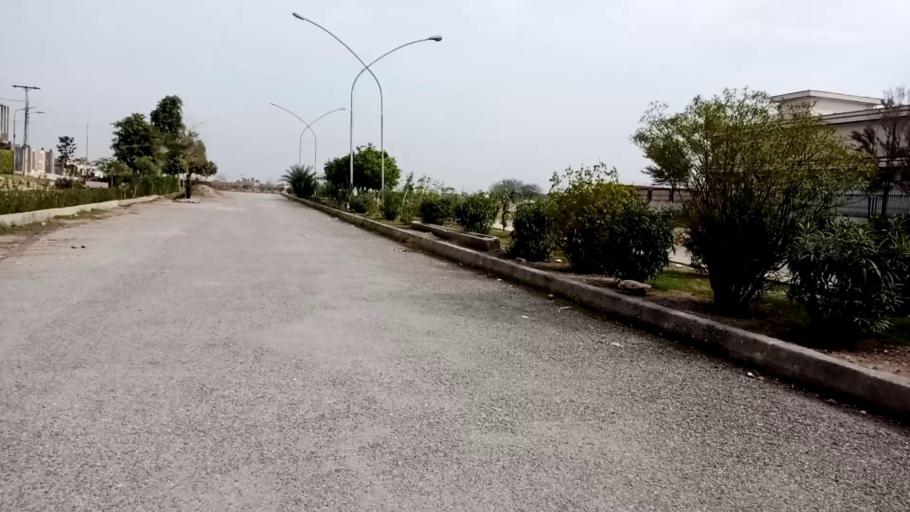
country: PK
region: Khyber Pakhtunkhwa
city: Peshawar
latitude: 33.9564
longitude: 71.4440
